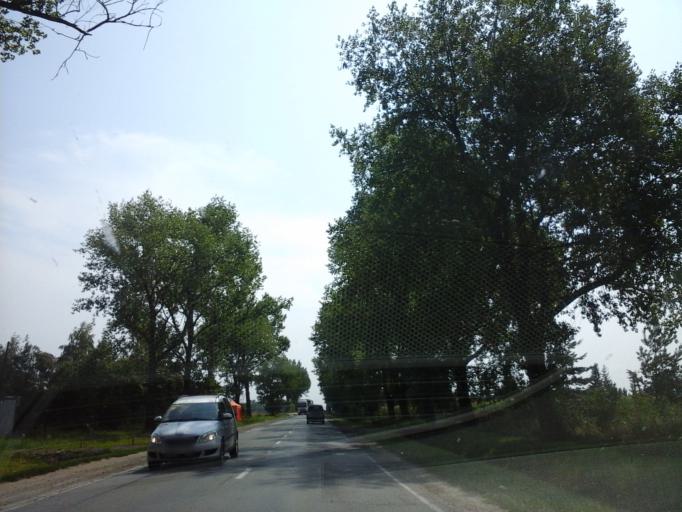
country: PL
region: Lower Silesian Voivodeship
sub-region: Powiat wroclawski
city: Zerniki Wroclawskie
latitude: 51.0469
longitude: 17.0603
